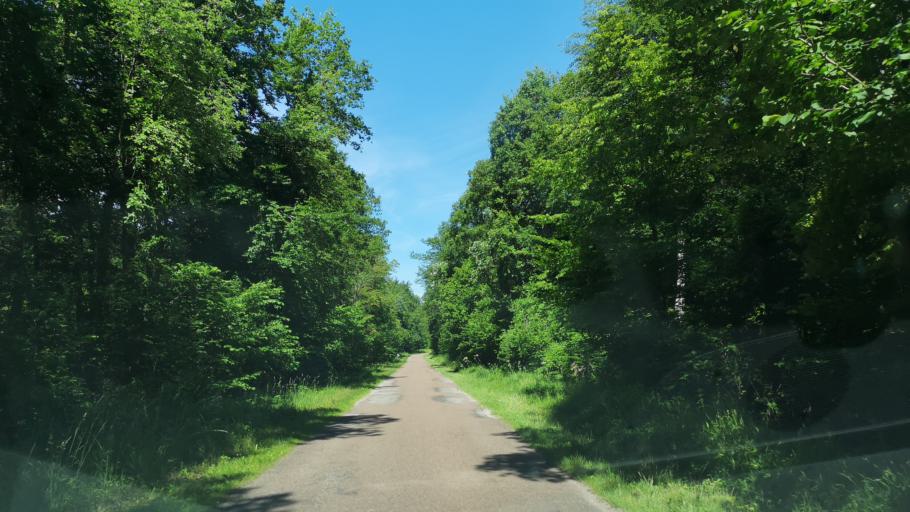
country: FR
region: Lorraine
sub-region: Departement de la Meuse
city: Vigneulles-les-Hattonchatel
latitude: 49.0277
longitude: 5.6463
